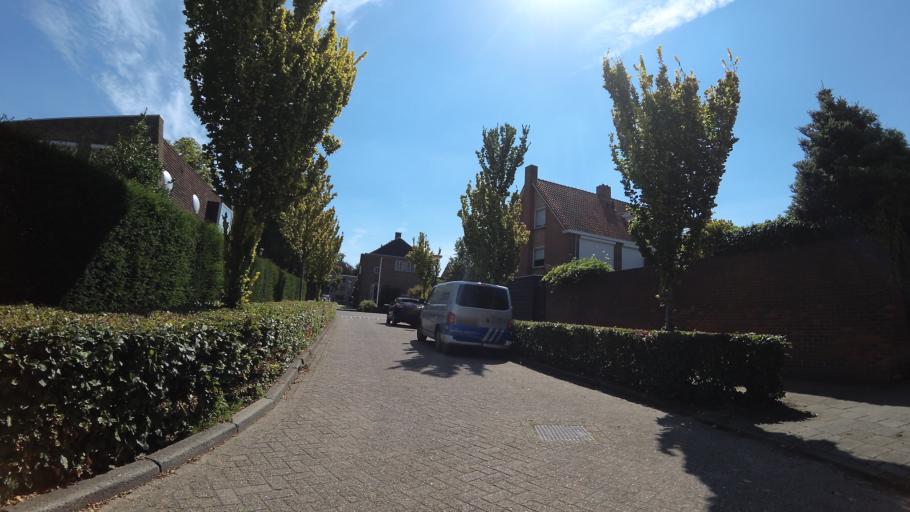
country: NL
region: North Brabant
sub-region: Gemeente Waalwijk
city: Waalwijk
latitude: 51.6570
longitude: 5.0443
